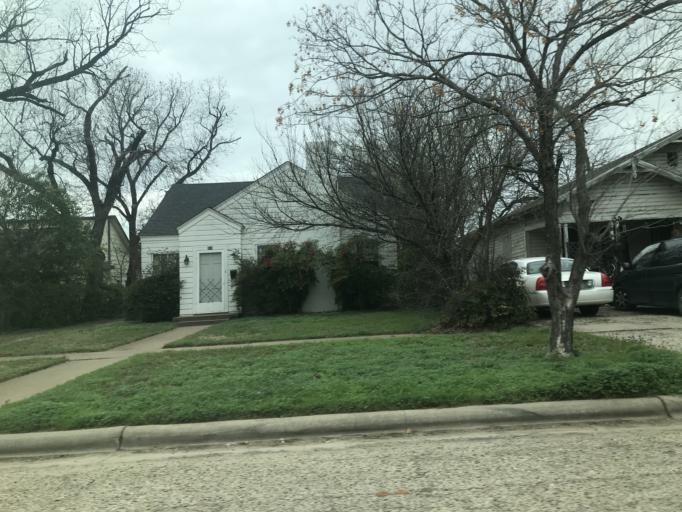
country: US
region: Texas
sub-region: Taylor County
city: Abilene
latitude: 32.4601
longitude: -99.7382
